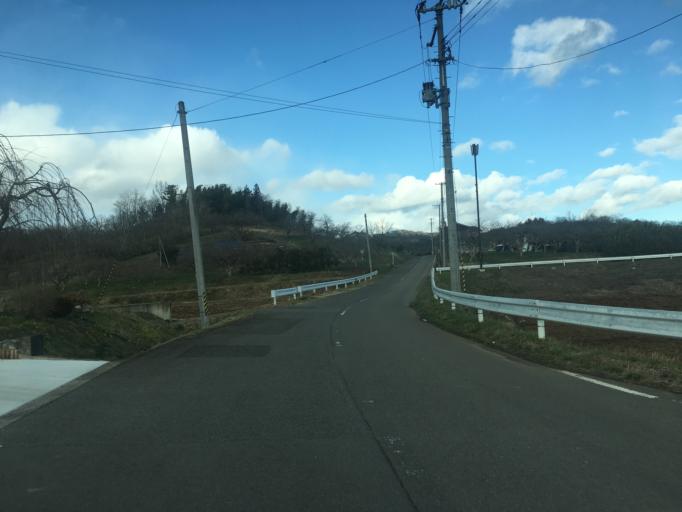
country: JP
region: Fukushima
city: Yanagawamachi-saiwaicho
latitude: 37.8797
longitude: 140.5976
